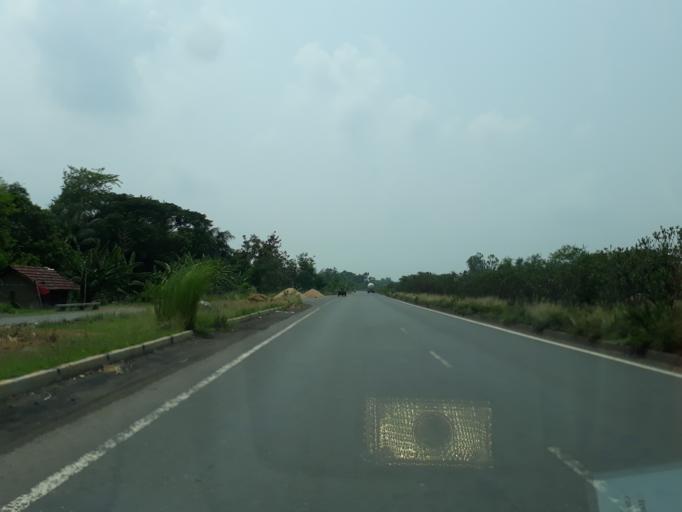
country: IN
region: West Bengal
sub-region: Purba Medinipur
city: Mahishadal
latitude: 22.1509
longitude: 87.9599
